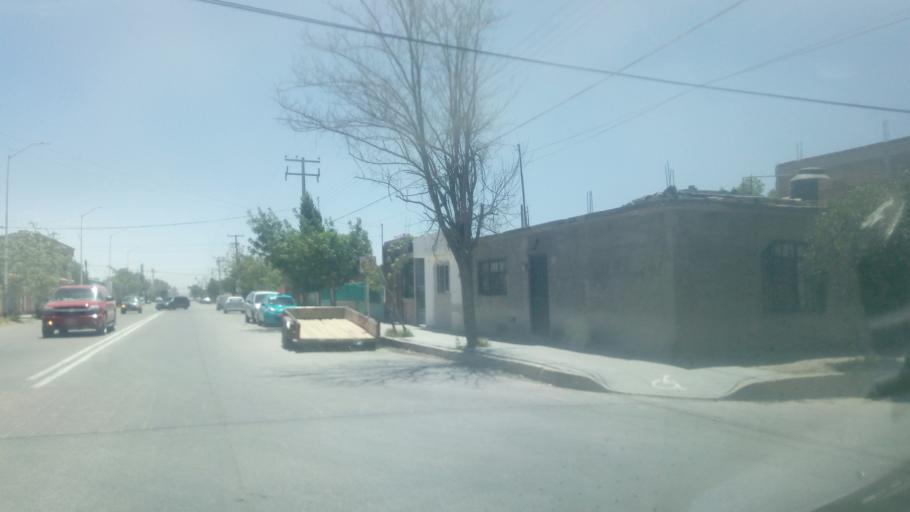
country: MX
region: Durango
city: Victoria de Durango
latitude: 24.0175
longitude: -104.6250
